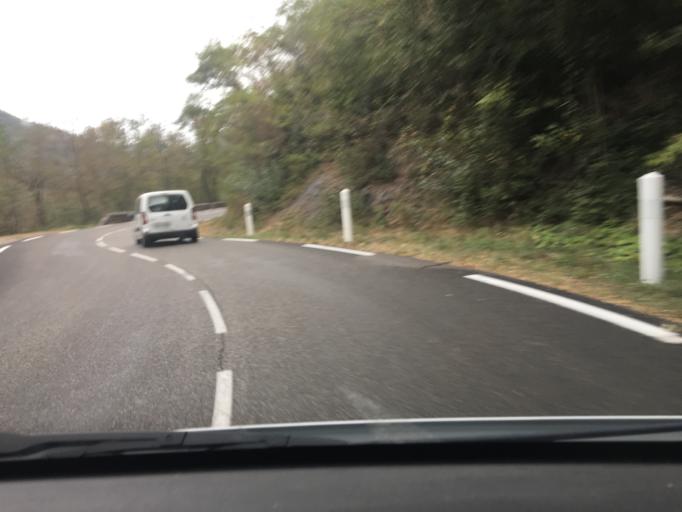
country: FR
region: Rhone-Alpes
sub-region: Departement de l'Ardeche
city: Saint-Jean-de-Muzols
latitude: 45.0564
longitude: 4.7745
